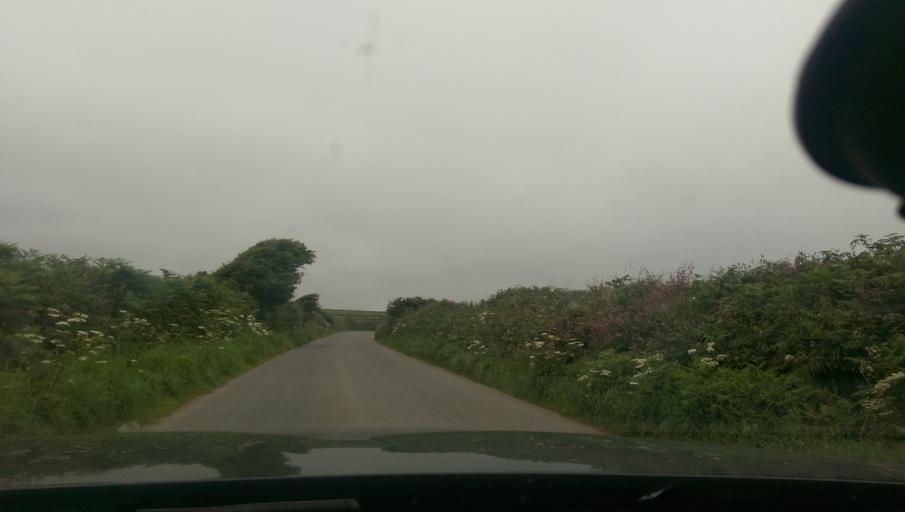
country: GB
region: England
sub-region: Cornwall
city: St. Buryan
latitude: 50.0920
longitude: -5.6438
